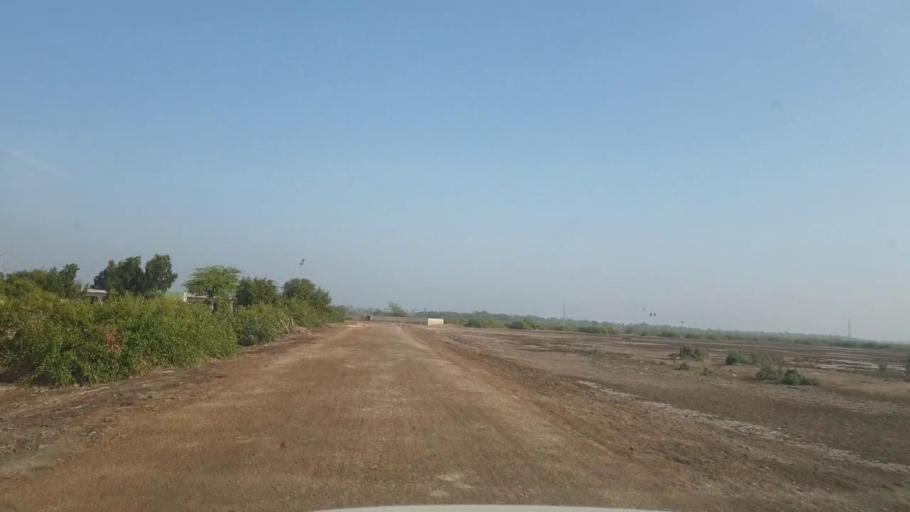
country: PK
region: Sindh
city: Mirpur Khas
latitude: 25.5047
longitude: 69.0478
